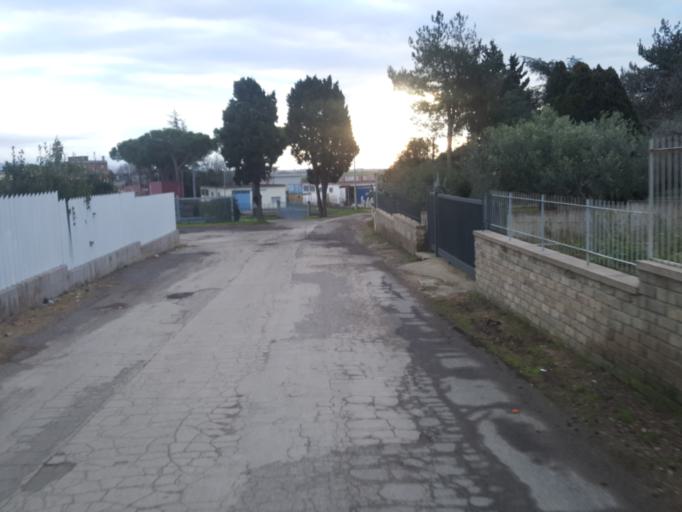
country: IT
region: Latium
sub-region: Citta metropolitana di Roma Capitale
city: Area Produttiva
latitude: 41.6985
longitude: 12.5413
